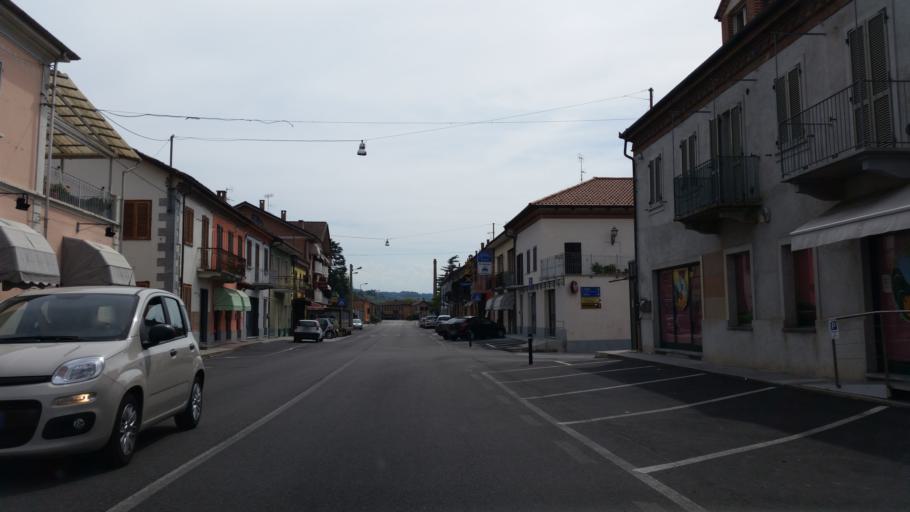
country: IT
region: Piedmont
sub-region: Provincia di Cuneo
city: Grinzane Cavour
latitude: 44.6550
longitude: 7.9801
